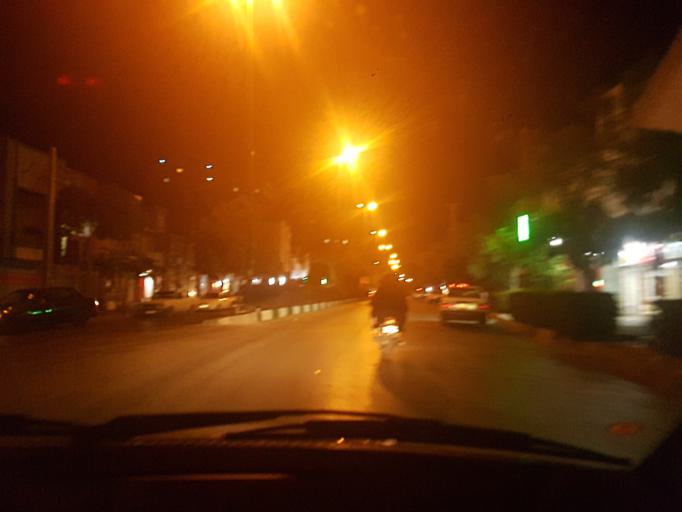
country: IR
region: Markazi
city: Arak
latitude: 34.0709
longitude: 49.6761
